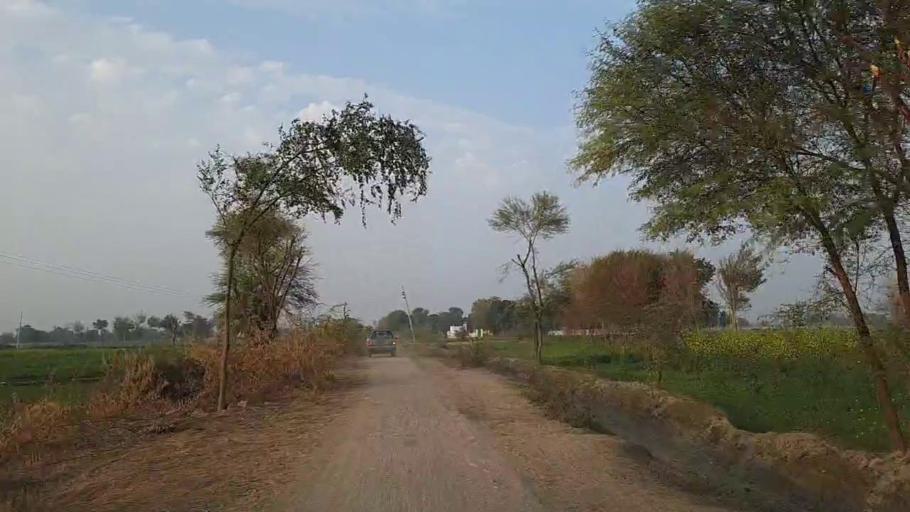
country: PK
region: Sindh
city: Jam Sahib
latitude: 26.3185
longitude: 68.6091
